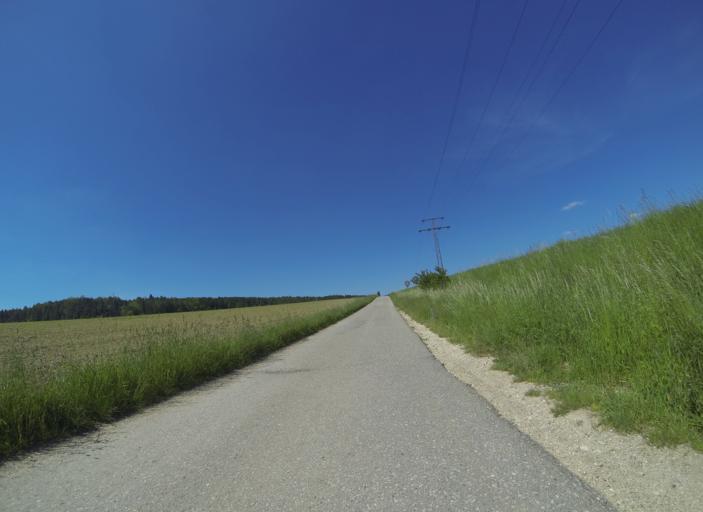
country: DE
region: Baden-Wuerttemberg
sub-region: Tuebingen Region
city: Allmendingen
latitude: 48.3401
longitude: 9.7304
